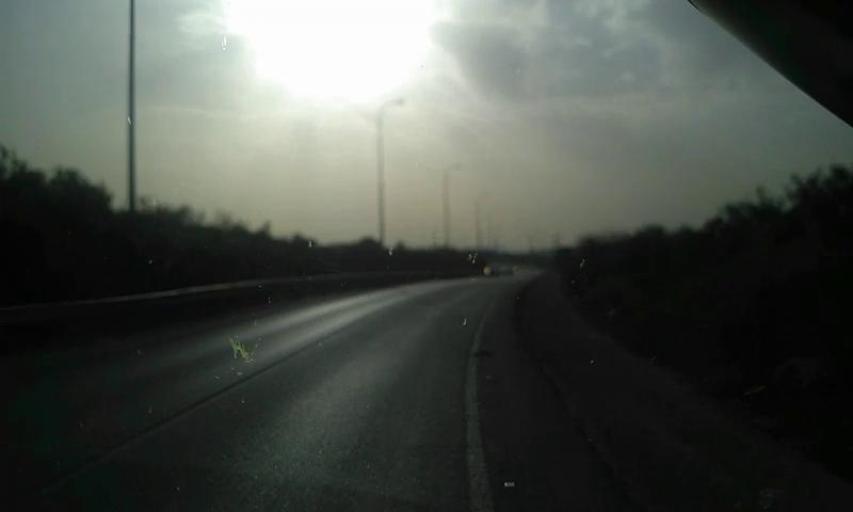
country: PS
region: West Bank
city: An Nabi Ilyas
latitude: 32.1866
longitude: 35.0047
